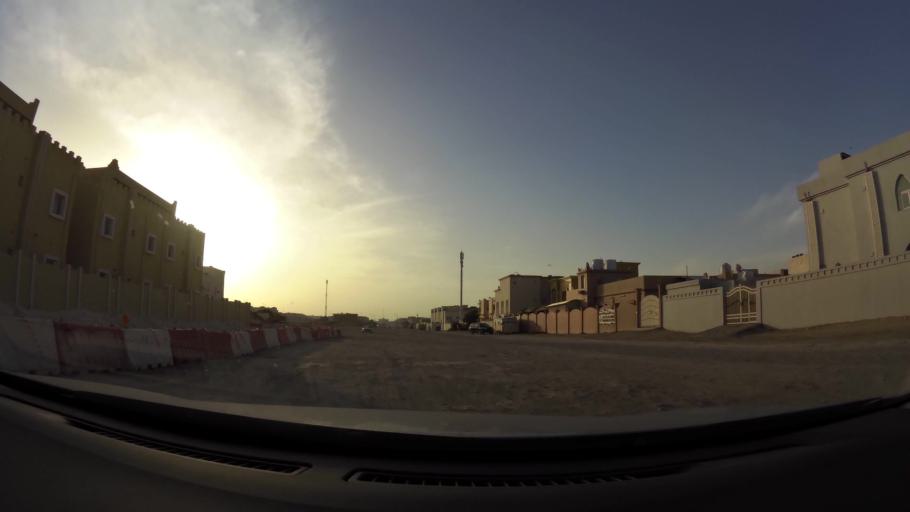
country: QA
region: Al Wakrah
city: Al Wakrah
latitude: 25.1479
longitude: 51.6092
